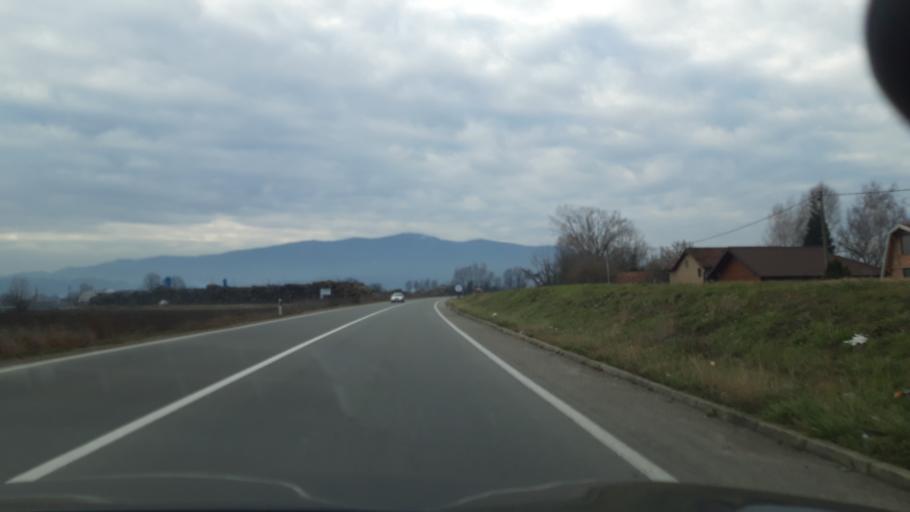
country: RS
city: Lipnicki Sor
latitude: 44.5534
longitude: 19.1986
